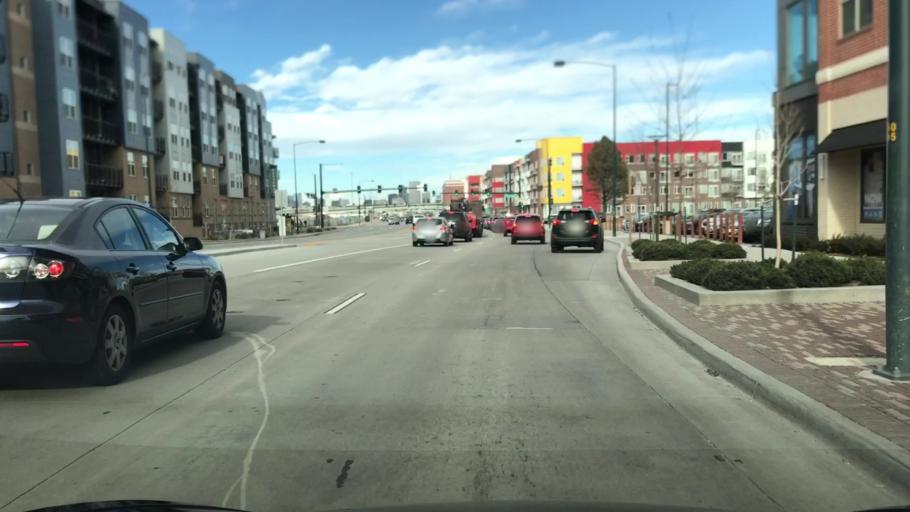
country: US
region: Colorado
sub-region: Denver County
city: Denver
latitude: 39.6952
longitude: -104.9874
